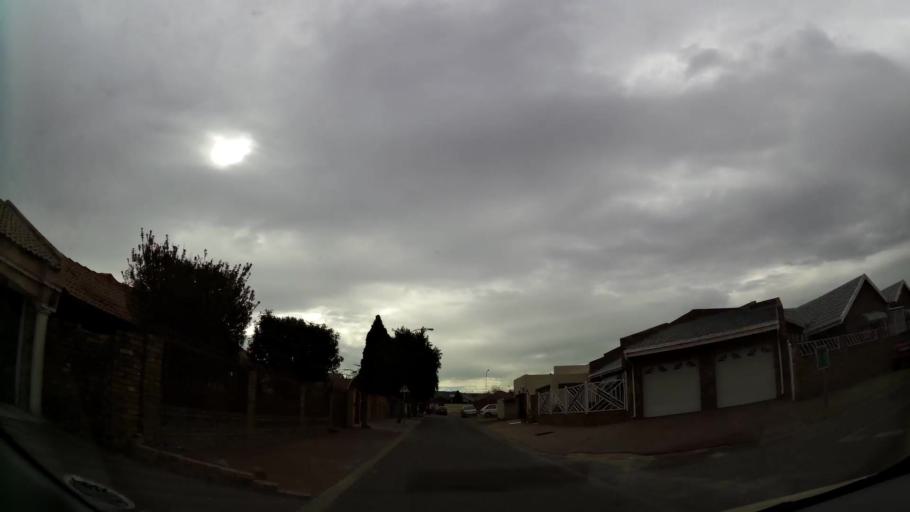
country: ZA
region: Gauteng
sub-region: City of Tshwane Metropolitan Municipality
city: Pretoria
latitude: -25.7087
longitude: 28.3258
